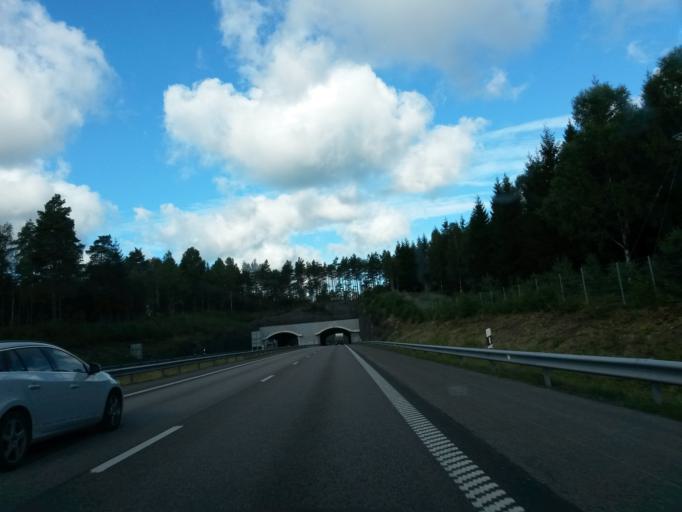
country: SE
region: Vaestra Goetaland
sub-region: Harryda Kommun
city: Landvetter
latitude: 57.7417
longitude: 12.1905
